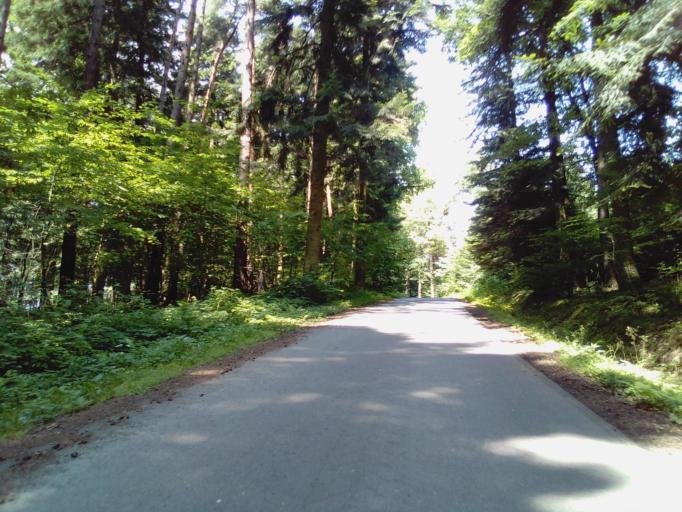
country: PL
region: Subcarpathian Voivodeship
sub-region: Powiat strzyzowski
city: Frysztak
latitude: 49.7897
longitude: 21.6029
